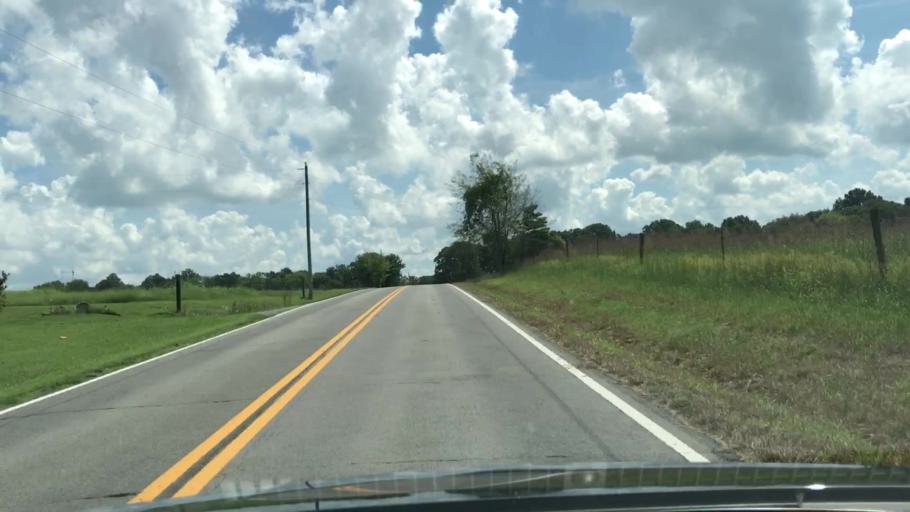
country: US
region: Tennessee
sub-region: Robertson County
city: Springfield
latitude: 36.5941
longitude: -86.9040
